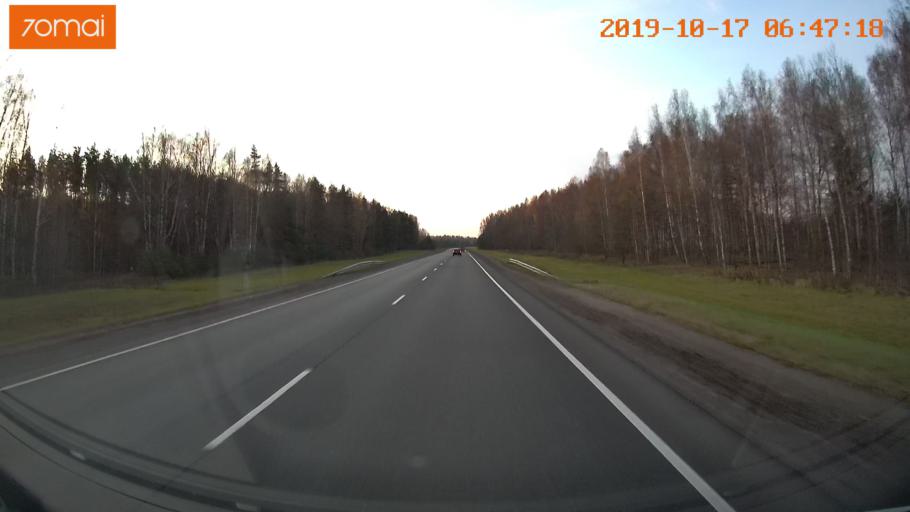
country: RU
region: Vladimir
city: Kideksha
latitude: 56.5381
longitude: 40.5562
